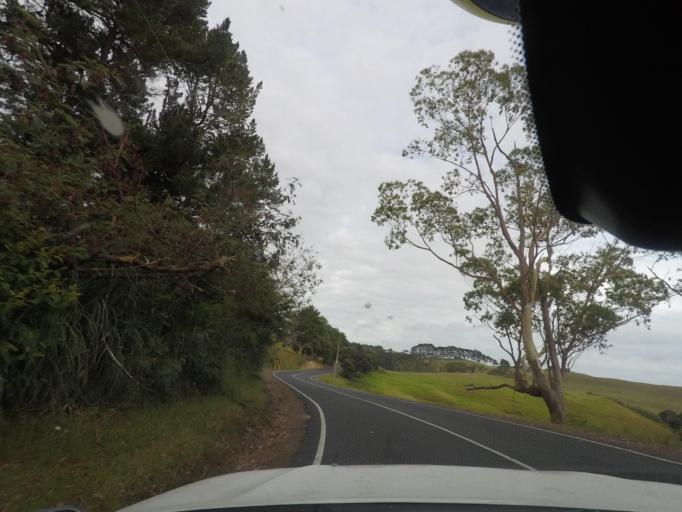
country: NZ
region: Auckland
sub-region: Auckland
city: Parakai
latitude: -36.5249
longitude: 174.2885
